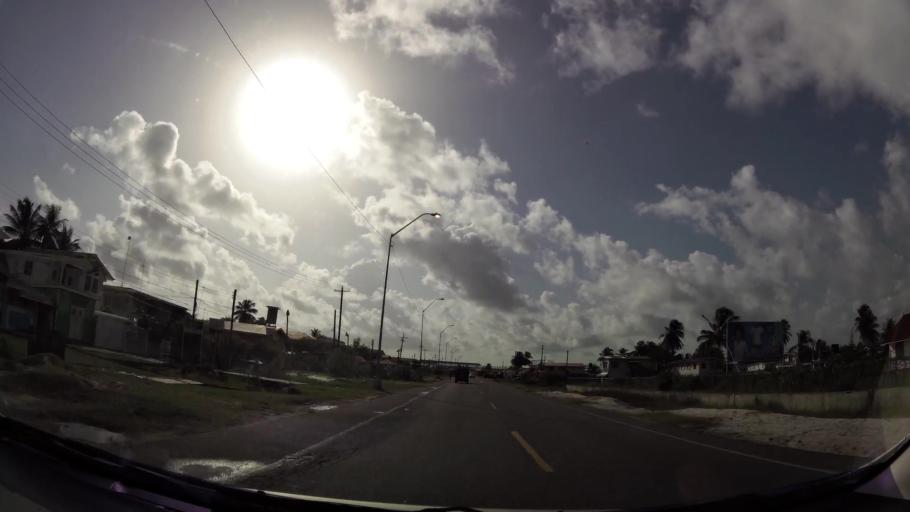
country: GY
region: Demerara-Mahaica
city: Georgetown
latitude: 6.8180
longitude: -58.0863
